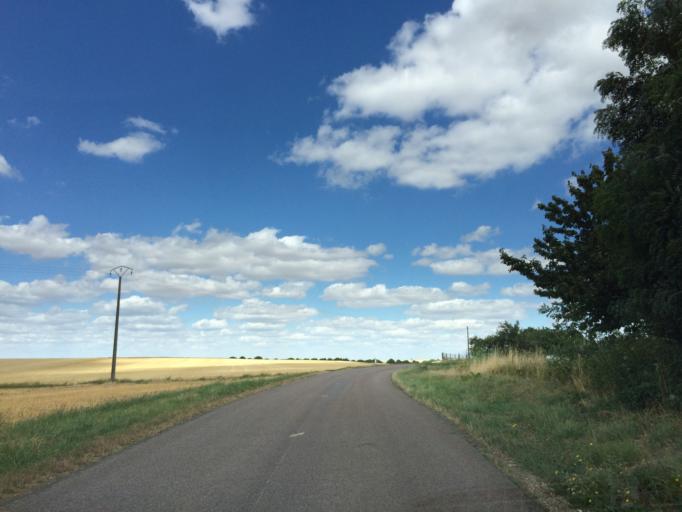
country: FR
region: Bourgogne
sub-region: Departement de l'Yonne
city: Fleury-la-Vallee
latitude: 47.8727
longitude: 3.4679
